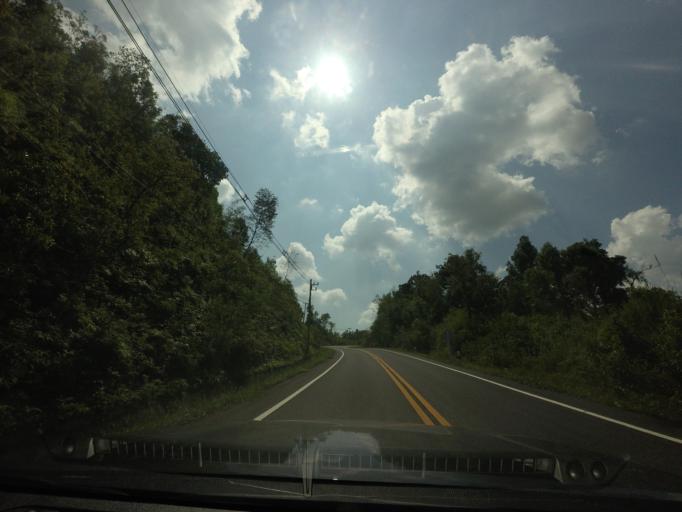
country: TH
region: Nan
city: Bo Kluea
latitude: 19.0782
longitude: 101.1424
